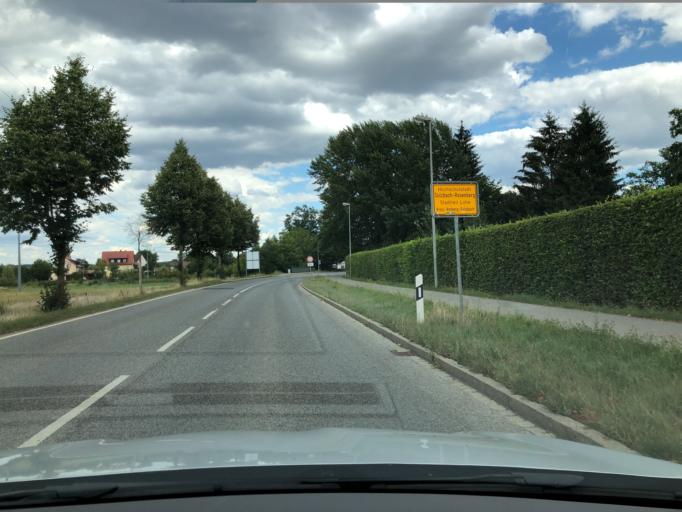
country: DE
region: Bavaria
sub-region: Upper Palatinate
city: Poppenricht
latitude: 49.4912
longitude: 11.7817
